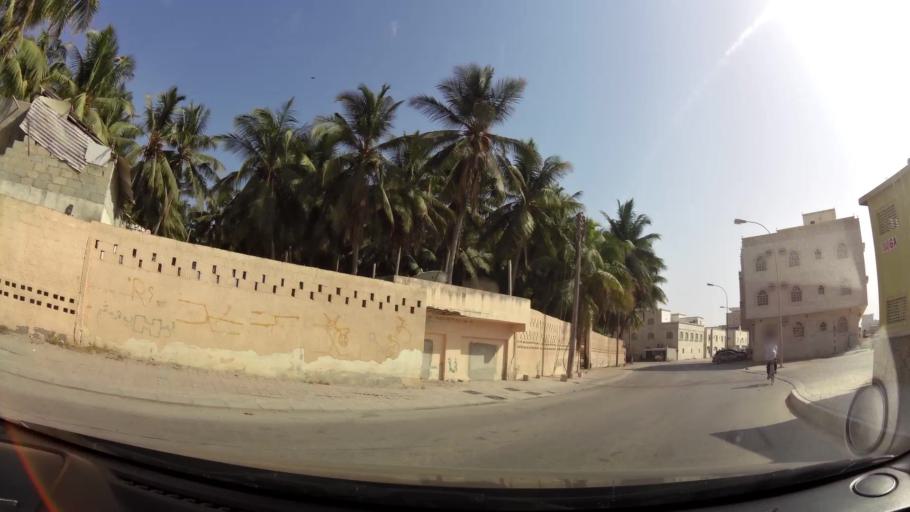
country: OM
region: Zufar
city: Salalah
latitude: 17.0001
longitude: 54.0395
